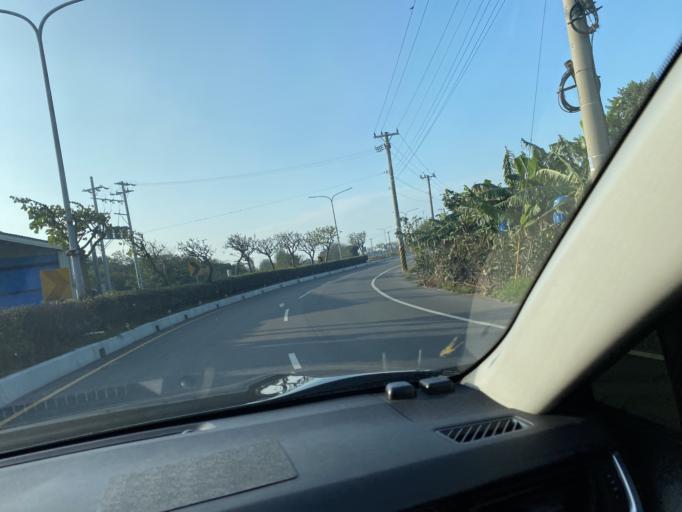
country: TW
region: Taiwan
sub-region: Changhua
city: Chang-hua
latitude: 23.9618
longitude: 120.3515
